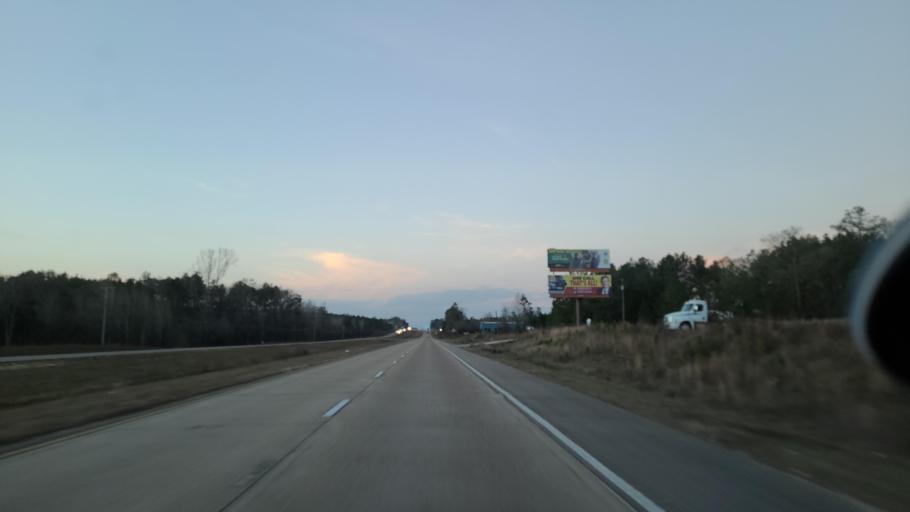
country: US
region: Mississippi
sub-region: Forrest County
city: Hattiesburg
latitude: 31.1759
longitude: -89.2467
